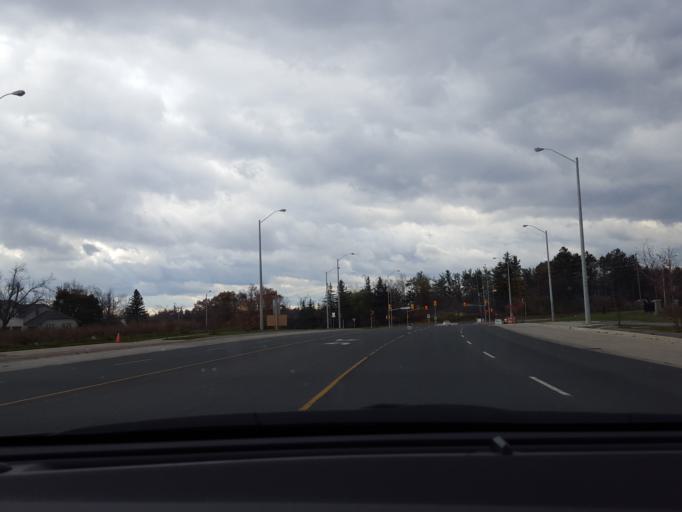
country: CA
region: Ontario
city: Brampton
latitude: 43.6487
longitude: -79.8010
